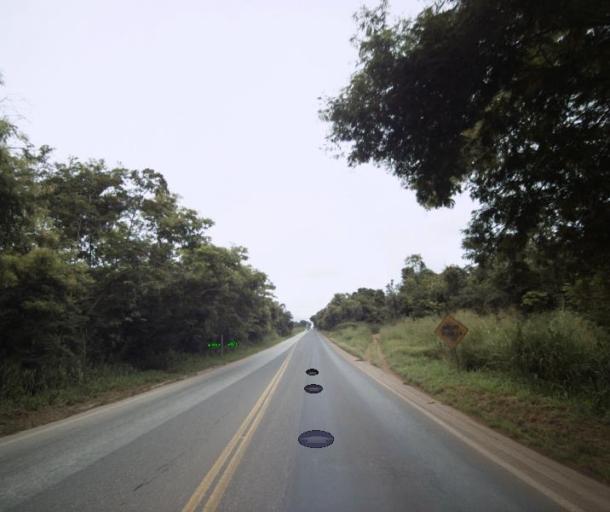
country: BR
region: Goias
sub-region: Uruacu
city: Uruacu
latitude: -14.5907
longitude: -49.1624
